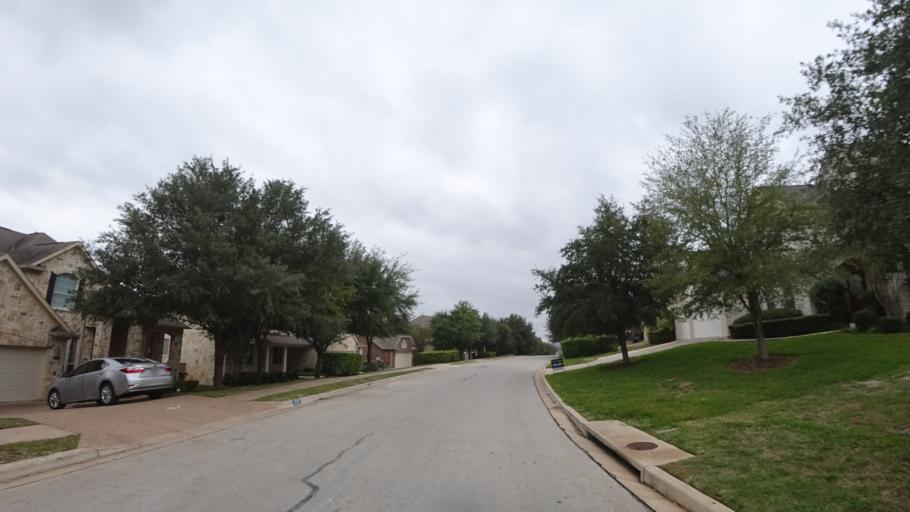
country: US
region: Texas
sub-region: Travis County
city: Hudson Bend
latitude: 30.3616
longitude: -97.8968
